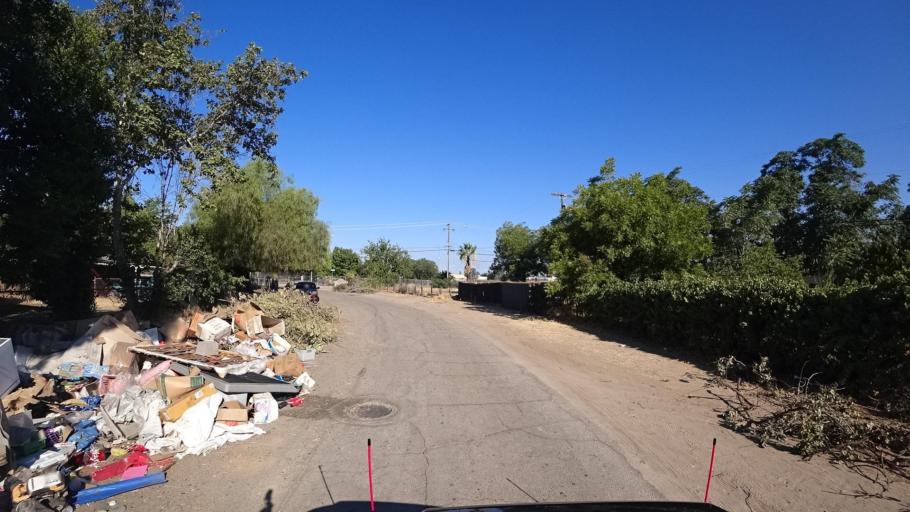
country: US
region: California
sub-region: Fresno County
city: Fresno
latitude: 36.7862
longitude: -119.7477
